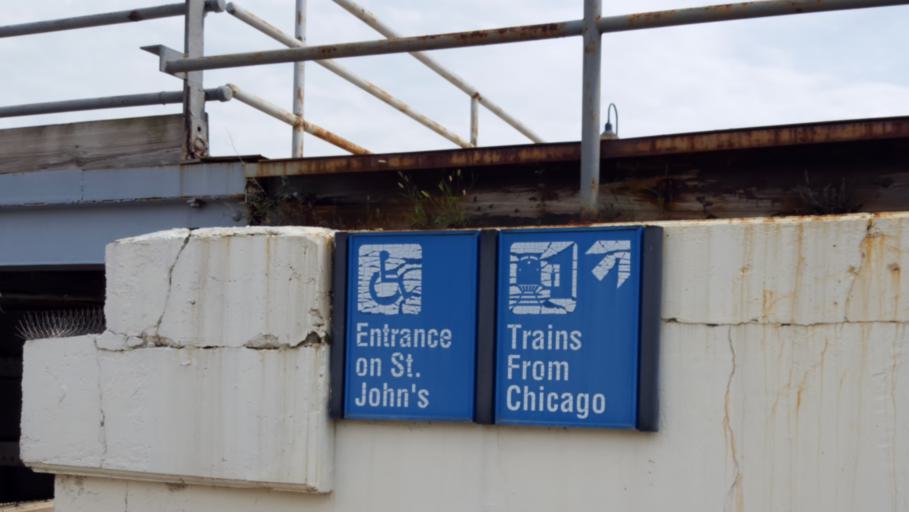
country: US
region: Illinois
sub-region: Lake County
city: Highland Park
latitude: 42.1842
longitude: -87.7985
